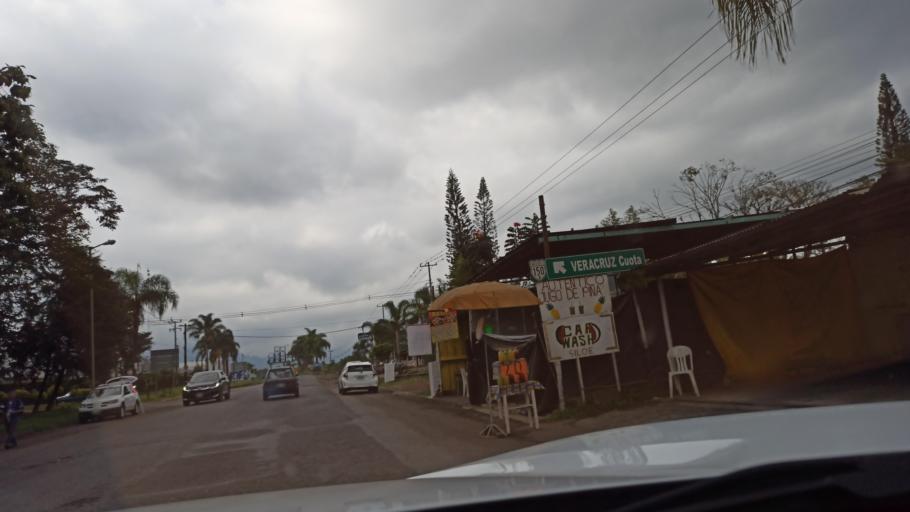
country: MX
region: Veracruz
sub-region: Fortin
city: Fortin de las Flores
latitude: 18.9121
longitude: -97.0008
